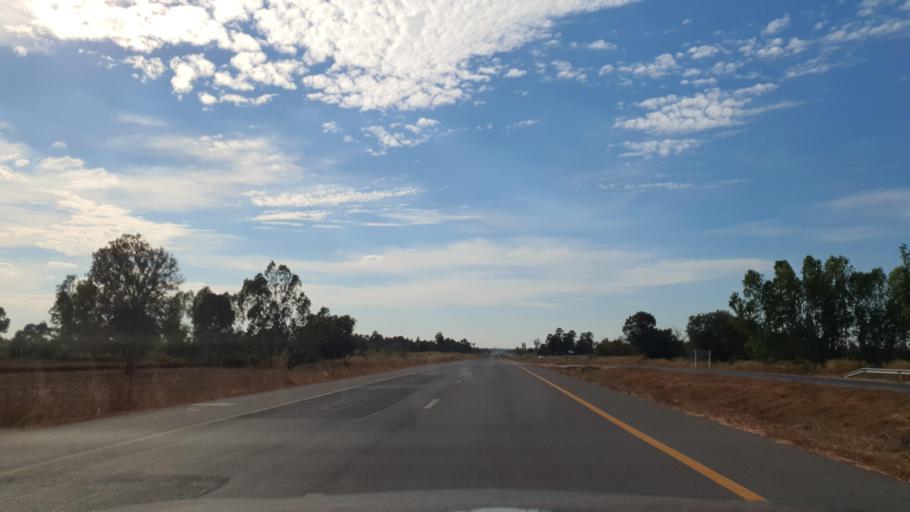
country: TH
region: Roi Et
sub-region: Amphoe Pho Chai
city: Pho Chai
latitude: 16.4134
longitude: 103.7822
